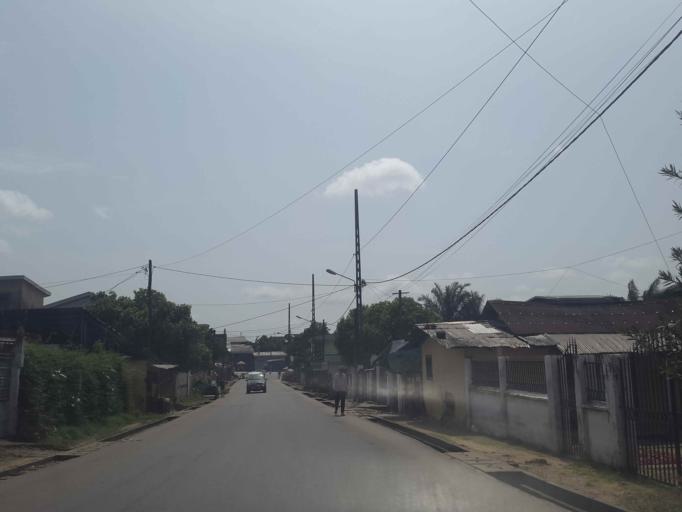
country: CM
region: Littoral
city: Douala
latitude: 4.0715
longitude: 9.7160
